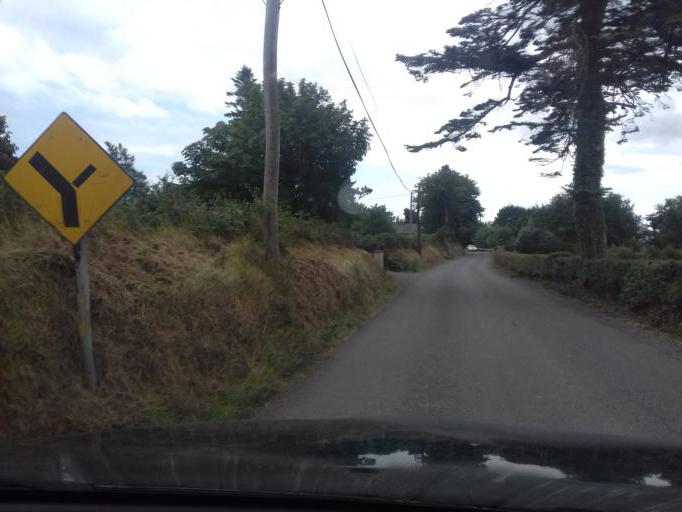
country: IE
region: Leinster
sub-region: Loch Garman
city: Castlebridge
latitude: 52.4075
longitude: -6.4080
